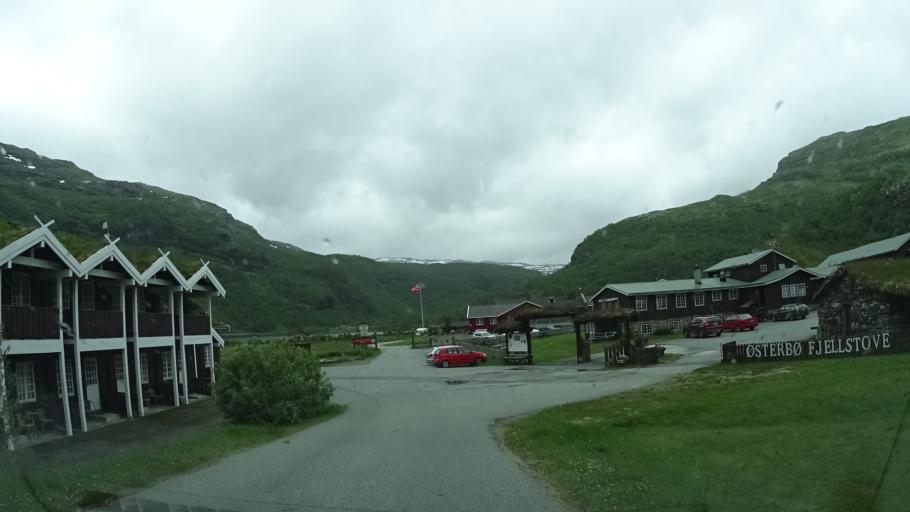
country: NO
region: Sogn og Fjordane
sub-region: Laerdal
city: Laerdalsoyri
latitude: 60.8284
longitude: 7.5069
